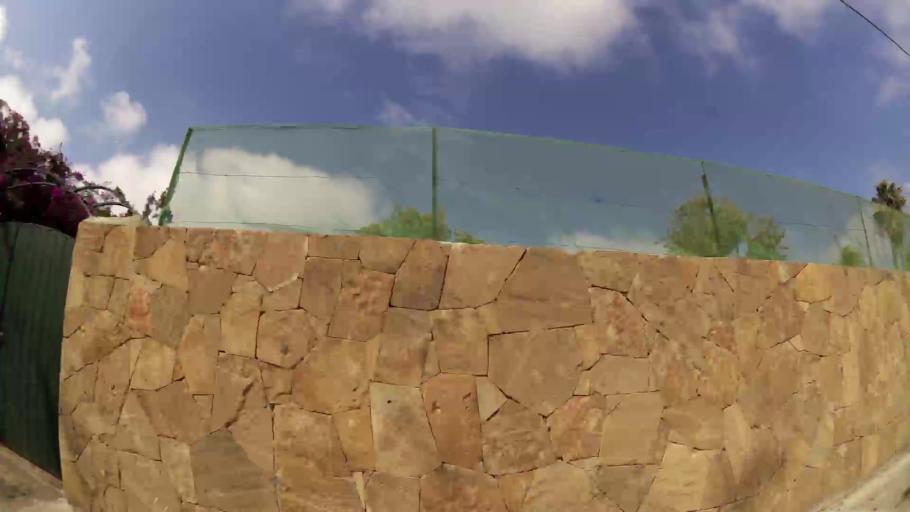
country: MA
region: Rabat-Sale-Zemmour-Zaer
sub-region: Rabat
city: Rabat
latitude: 33.9768
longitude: -6.8446
